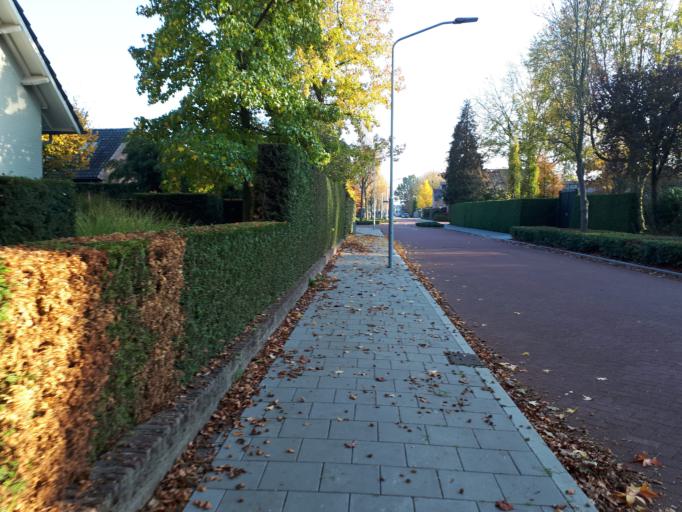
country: NL
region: North Brabant
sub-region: Gemeente Eersel
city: Eersel
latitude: 51.3626
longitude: 5.3176
